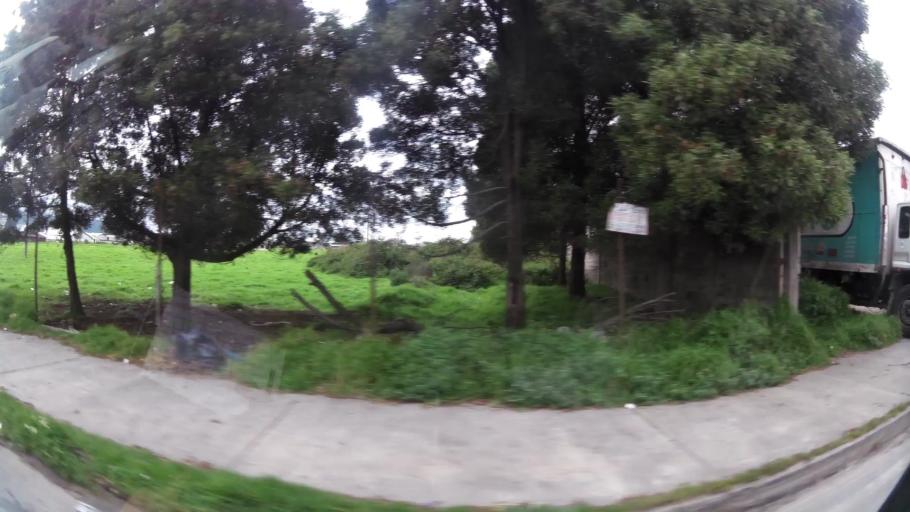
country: EC
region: Pichincha
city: Quito
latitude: -0.3180
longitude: -78.5451
